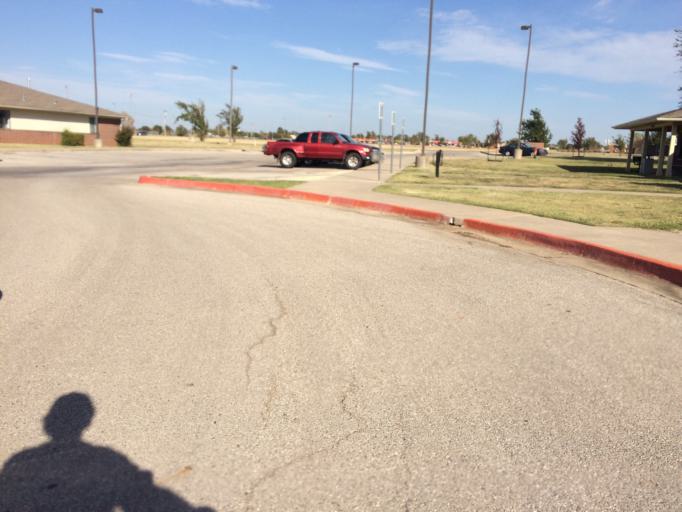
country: US
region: Oklahoma
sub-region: Cleveland County
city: Norman
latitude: 35.2314
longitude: -97.4306
